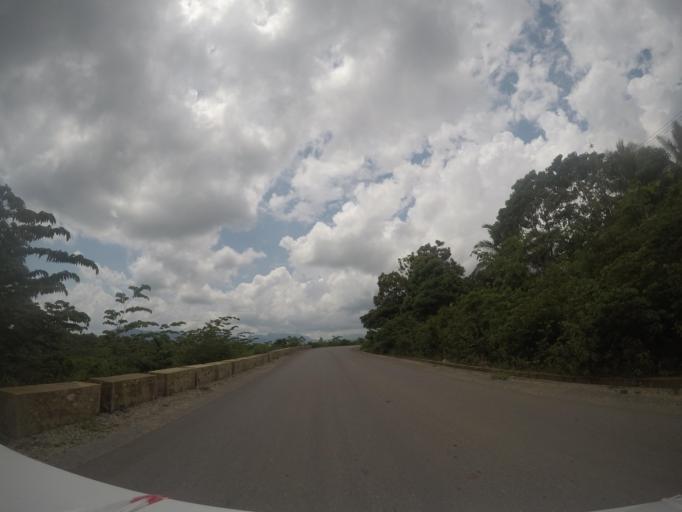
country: TL
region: Baucau
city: Venilale
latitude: -8.5577
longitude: 126.4031
